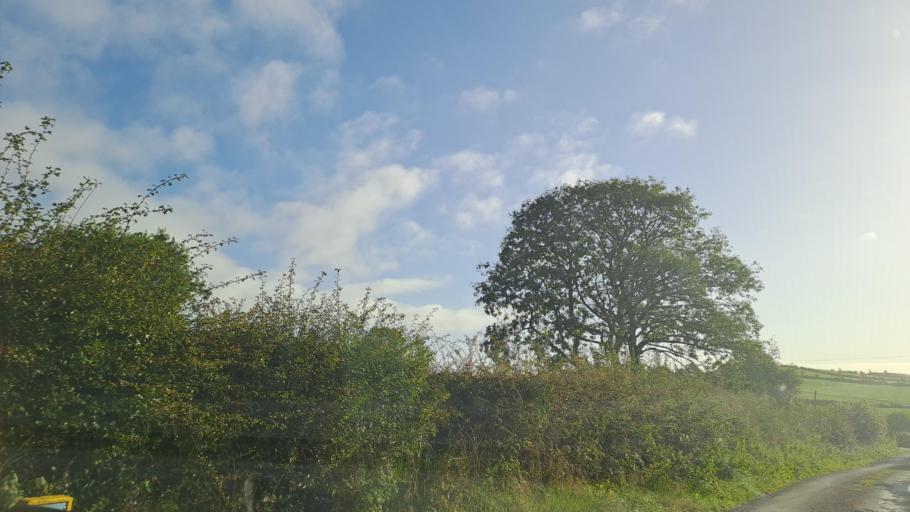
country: IE
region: Ulster
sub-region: An Cabhan
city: Kingscourt
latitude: 53.9478
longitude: -6.8766
